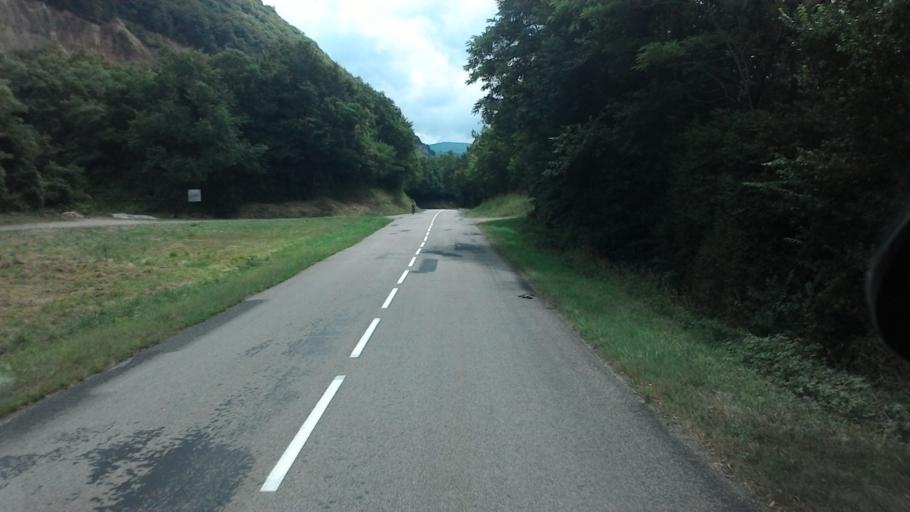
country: FR
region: Rhone-Alpes
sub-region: Departement de l'Ain
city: Saint-Sorlin-en-Bugey
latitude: 45.8773
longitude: 5.3971
